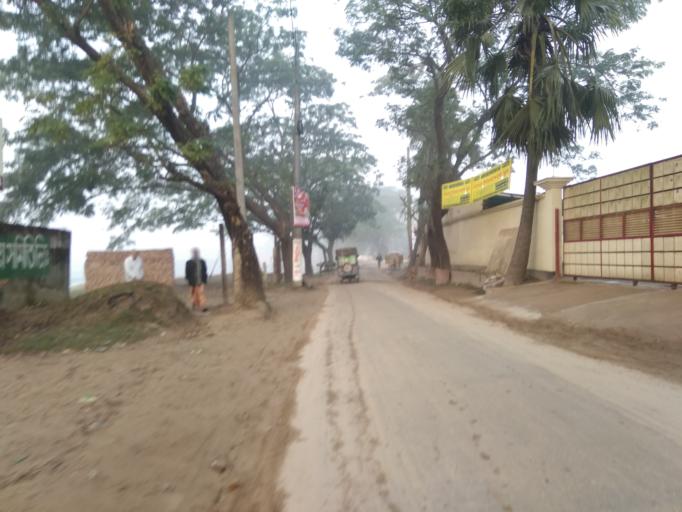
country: BD
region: Dhaka
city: Tungi
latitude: 23.8614
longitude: 90.4488
